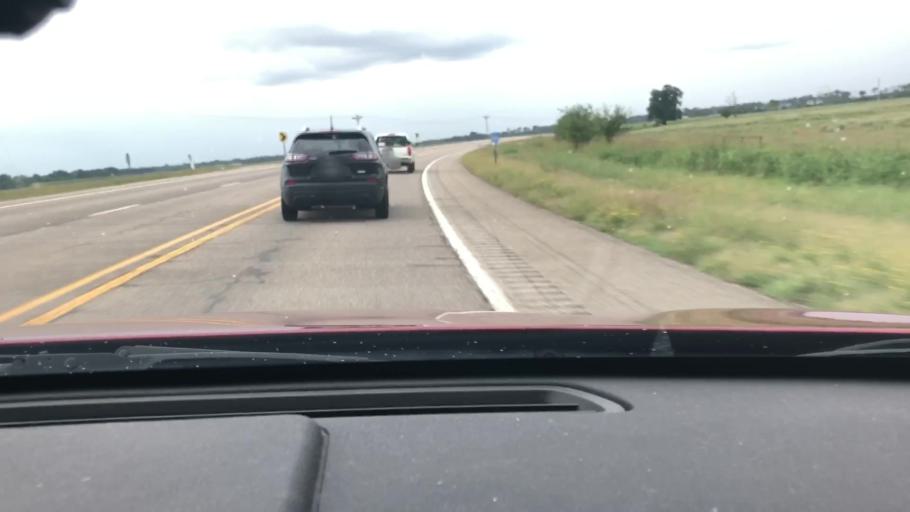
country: US
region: Arkansas
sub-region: Lafayette County
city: Lewisville
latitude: 33.3909
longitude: -93.7364
